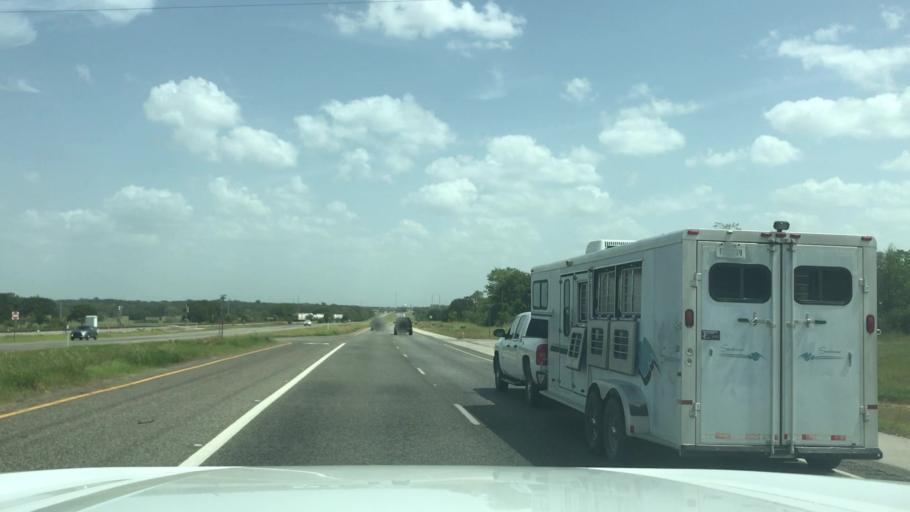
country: US
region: Texas
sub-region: Robertson County
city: Hearne
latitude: 30.9228
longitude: -96.6251
